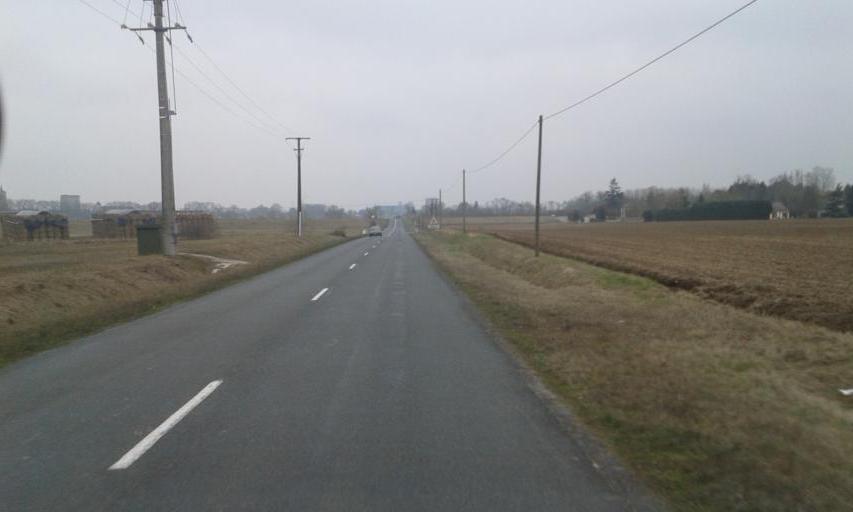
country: FR
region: Centre
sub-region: Departement du Loiret
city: Beaugency
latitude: 47.7671
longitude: 1.6421
